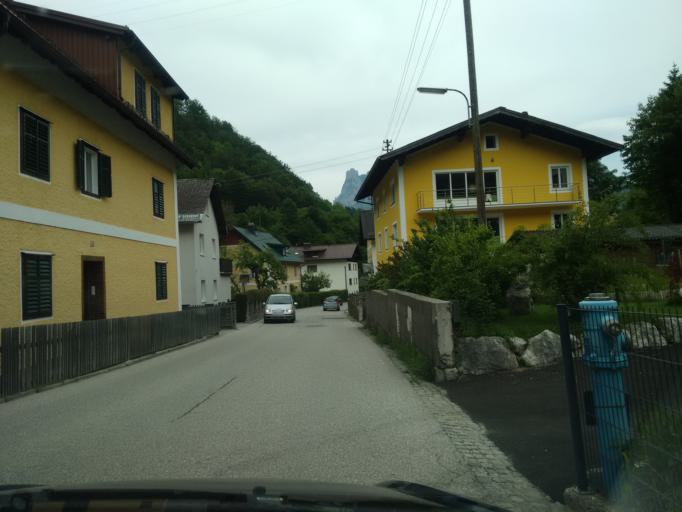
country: AT
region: Upper Austria
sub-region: Politischer Bezirk Gmunden
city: Ebensee
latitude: 47.8142
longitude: 13.7636
